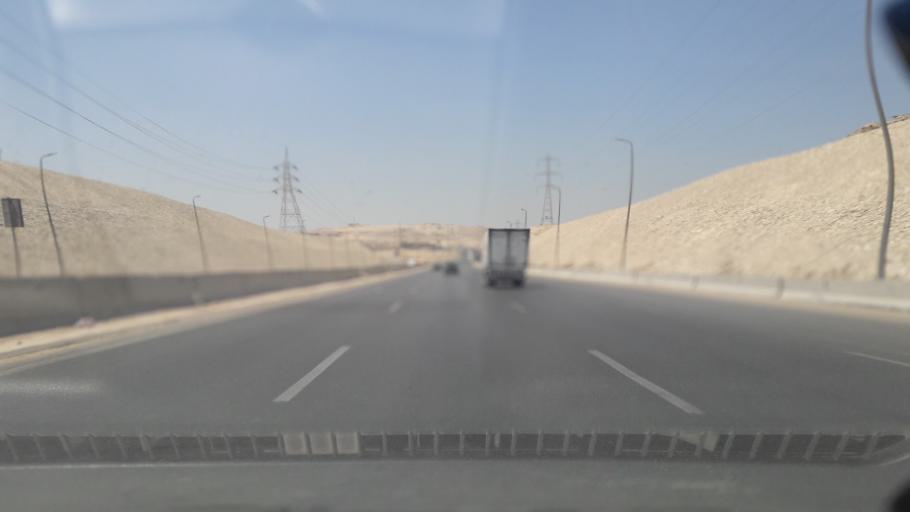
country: EG
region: Al Jizah
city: Awsim
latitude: 30.0106
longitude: 31.0860
